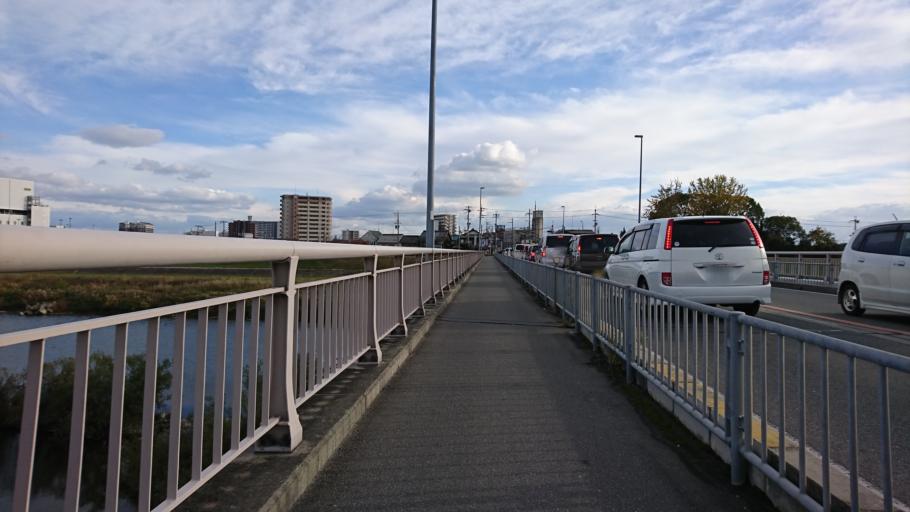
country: JP
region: Hyogo
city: Kakogawacho-honmachi
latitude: 34.7721
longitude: 134.8287
